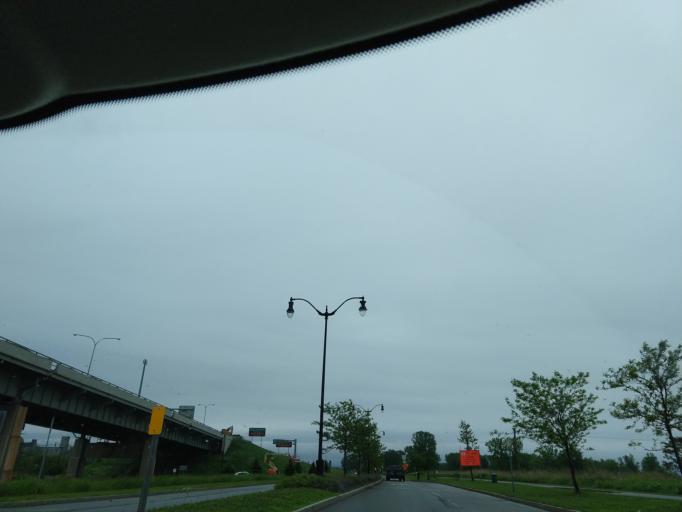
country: US
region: New York
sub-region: Erie County
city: Buffalo
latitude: 42.8678
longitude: -78.8781
